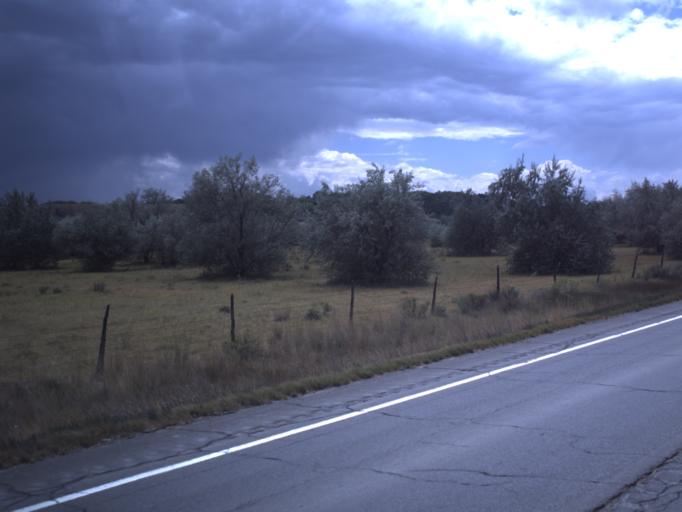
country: US
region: Utah
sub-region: Duchesne County
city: Roosevelt
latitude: 40.1809
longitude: -110.1100
